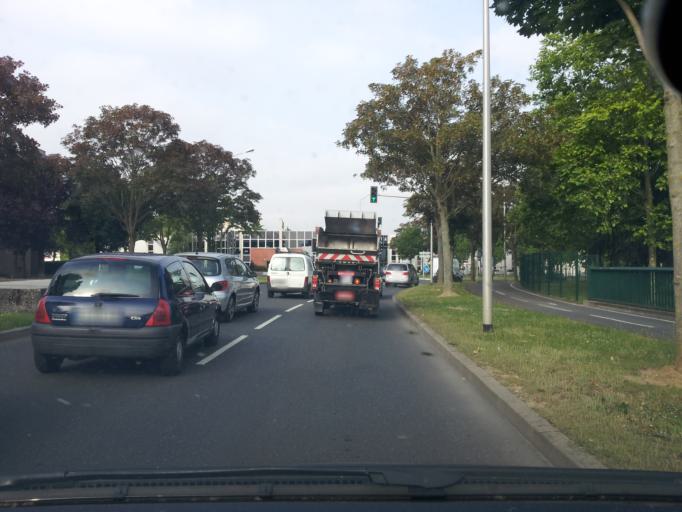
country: FR
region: Ile-de-France
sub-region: Departement de l'Essonne
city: Evry
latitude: 48.6214
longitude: 2.4458
